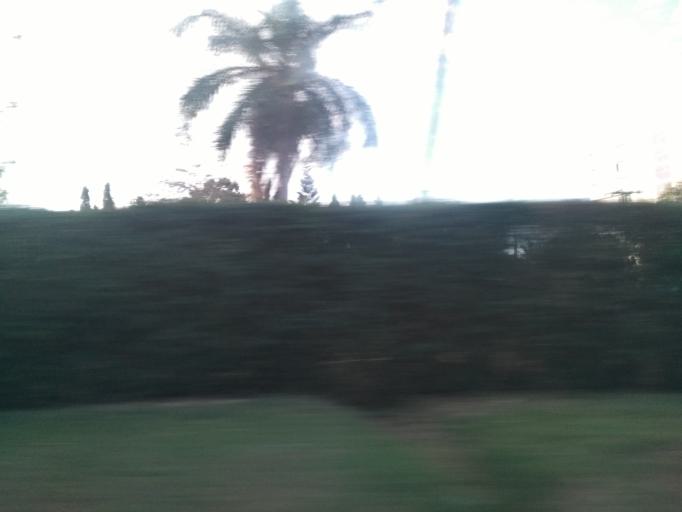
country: TZ
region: Dar es Salaam
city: Magomeni
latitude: -6.7833
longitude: 39.2743
